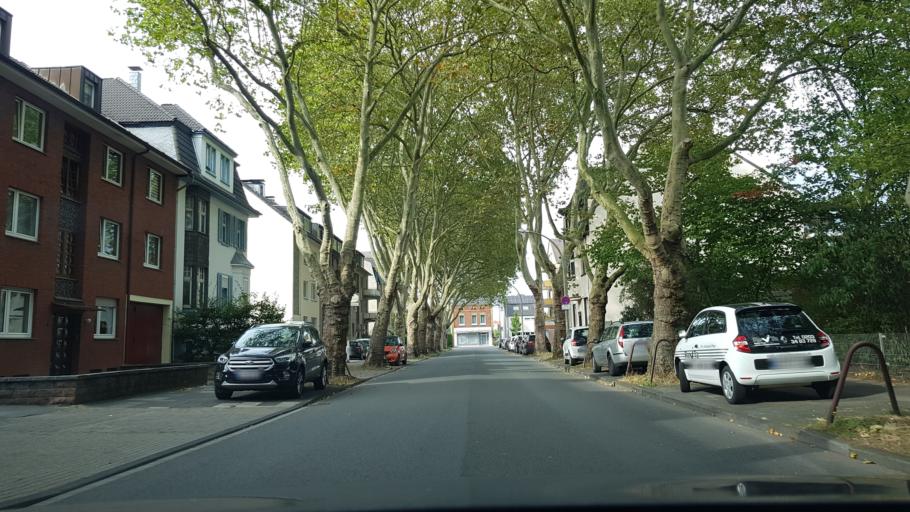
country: DE
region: North Rhine-Westphalia
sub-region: Regierungsbezirk Dusseldorf
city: Hochfeld
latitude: 51.3640
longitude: 6.7813
